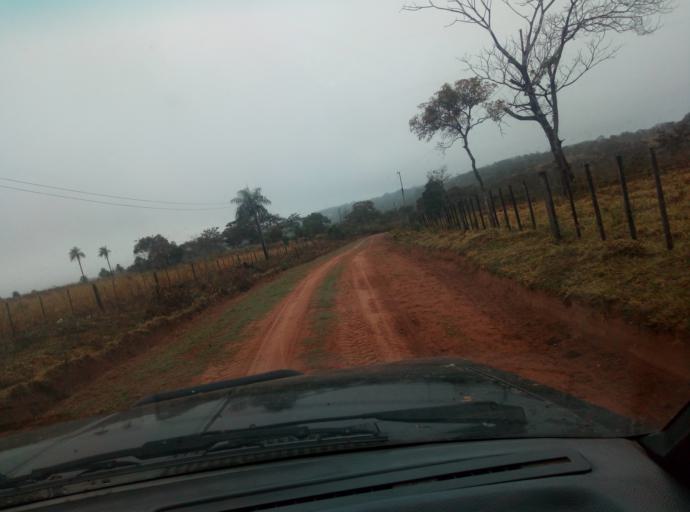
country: PY
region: Caaguazu
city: Carayao
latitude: -25.1922
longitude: -56.3205
